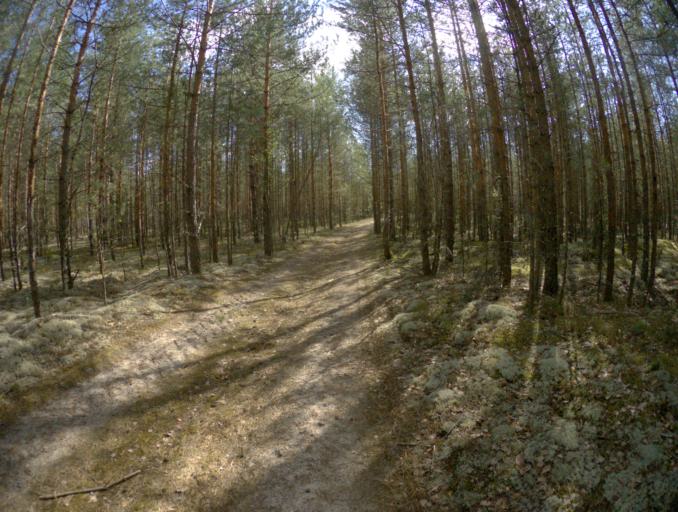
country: RU
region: Vladimir
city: Golovino
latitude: 55.8841
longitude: 40.3875
